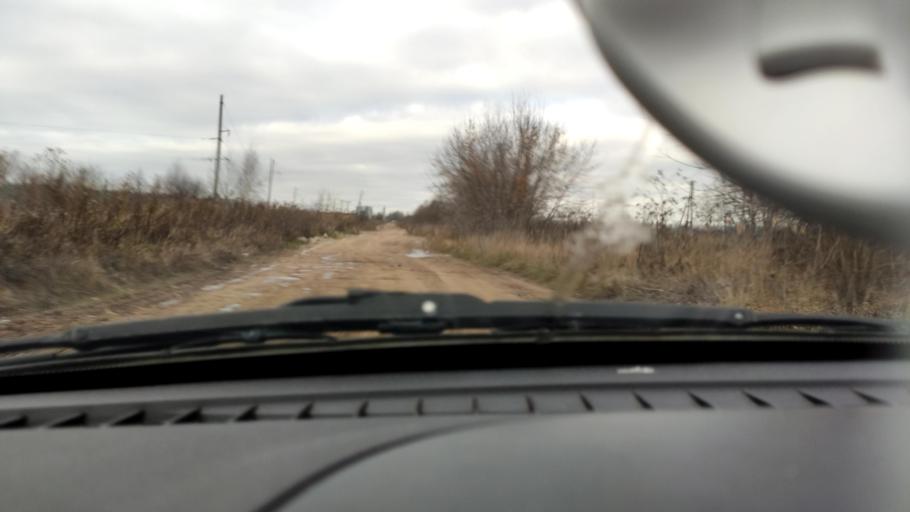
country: RU
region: Perm
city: Kondratovo
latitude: 57.9875
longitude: 56.0797
